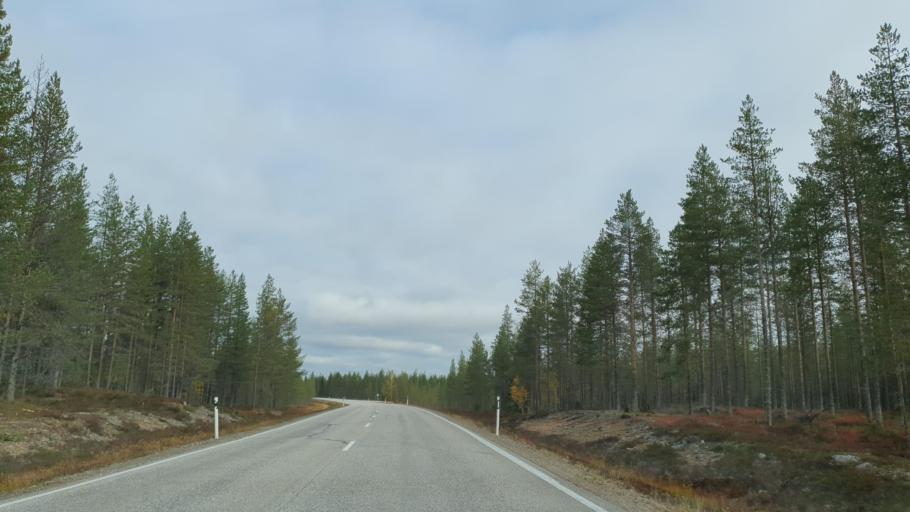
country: FI
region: Northern Ostrobothnia
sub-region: Oulunkaari
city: Pudasjaervi
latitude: 65.5373
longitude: 26.7646
